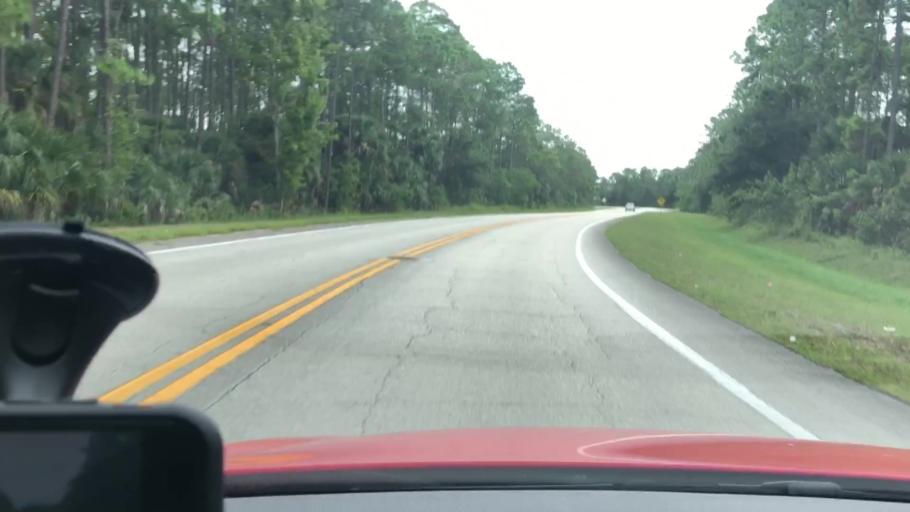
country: US
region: Florida
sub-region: Volusia County
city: Daytona Beach
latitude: 29.2030
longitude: -81.0791
